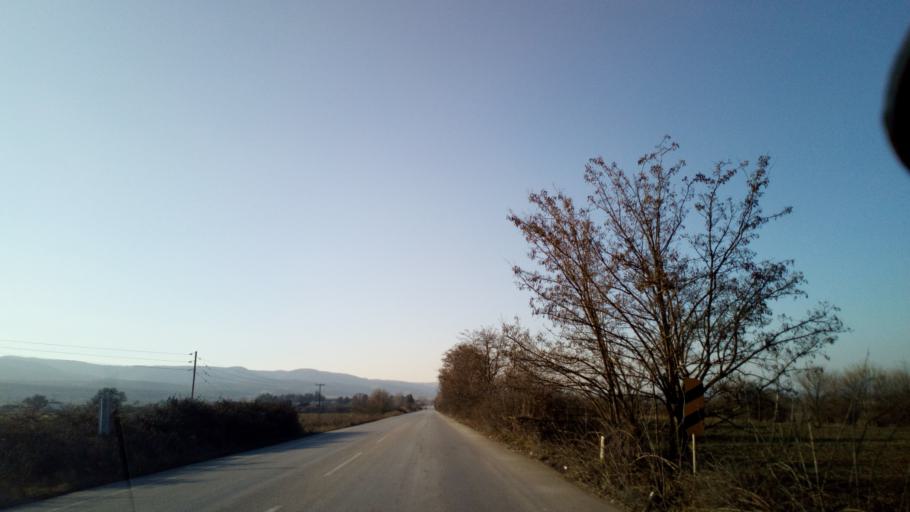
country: GR
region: Central Macedonia
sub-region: Nomos Thessalonikis
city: Agios Vasileios
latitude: 40.6679
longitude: 23.1044
